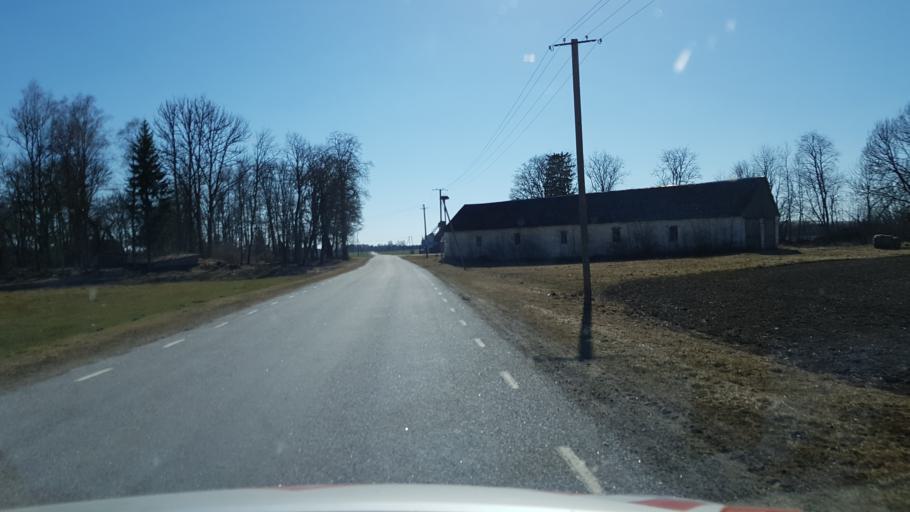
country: EE
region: Laeaene-Virumaa
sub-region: Tamsalu vald
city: Tamsalu
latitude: 59.0694
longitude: 26.1147
